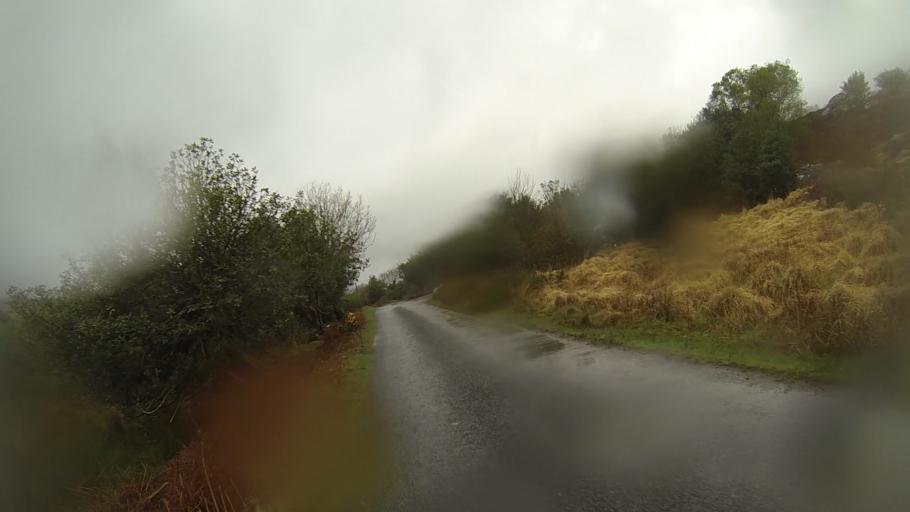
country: IE
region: Munster
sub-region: Ciarrai
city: Kenmare
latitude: 51.9497
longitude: -9.6535
